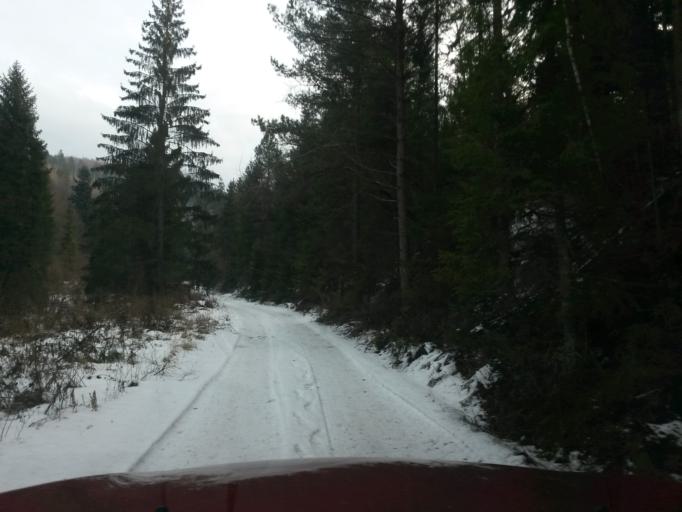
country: SK
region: Kosicky
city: Spisska Nova Ves
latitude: 48.8940
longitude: 20.6327
